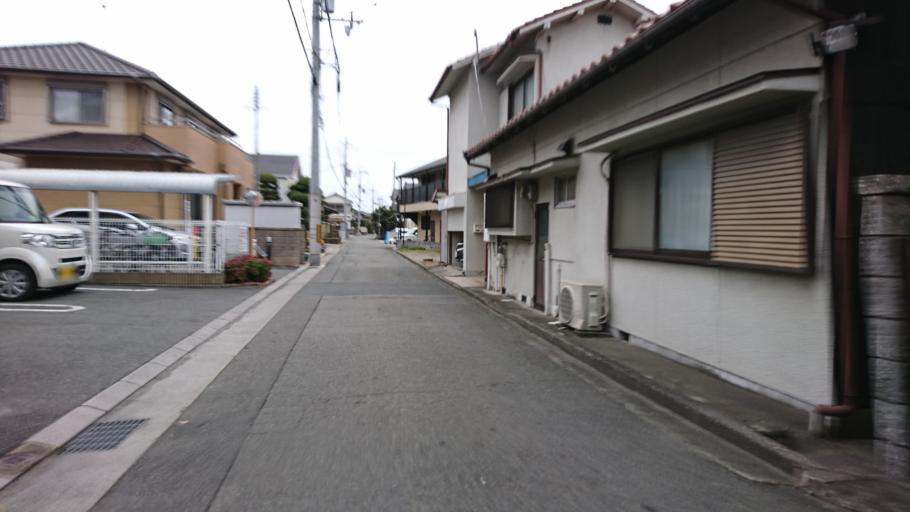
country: JP
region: Hyogo
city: Kakogawacho-honmachi
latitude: 34.7461
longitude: 134.8583
